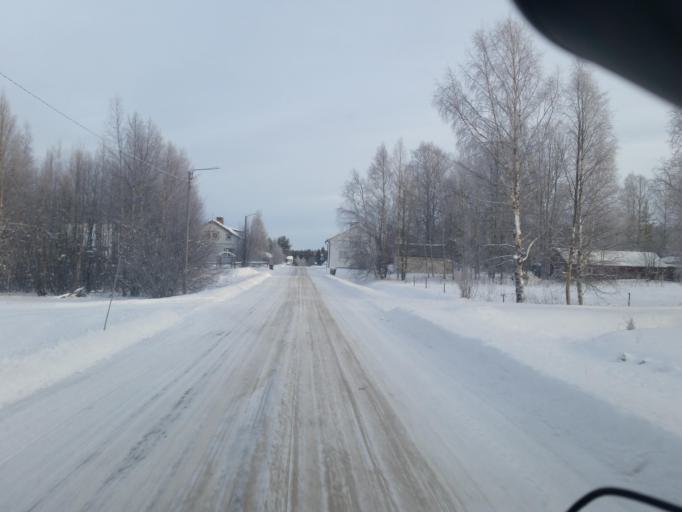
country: SE
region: Norrbotten
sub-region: Pitea Kommun
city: Rosvik
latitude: 65.3903
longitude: 21.7315
